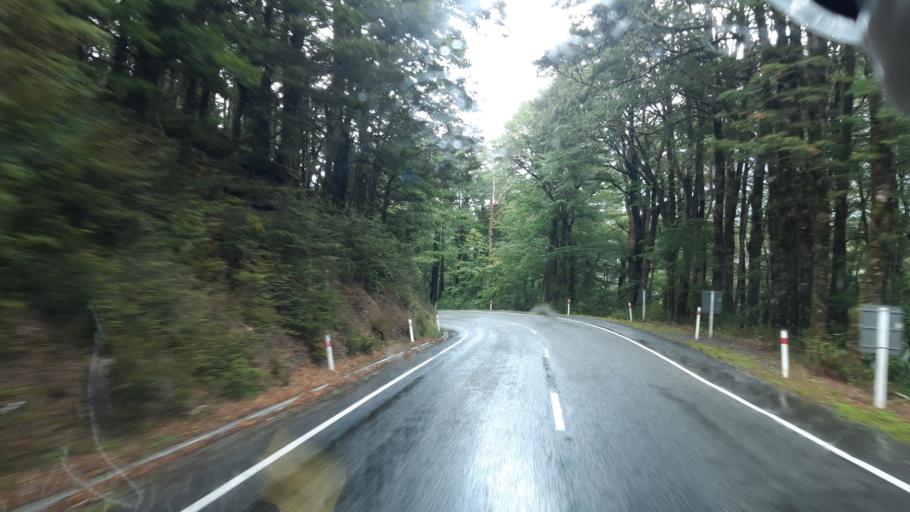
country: NZ
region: Canterbury
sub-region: Hurunui District
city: Amberley
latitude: -42.3763
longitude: 172.3599
